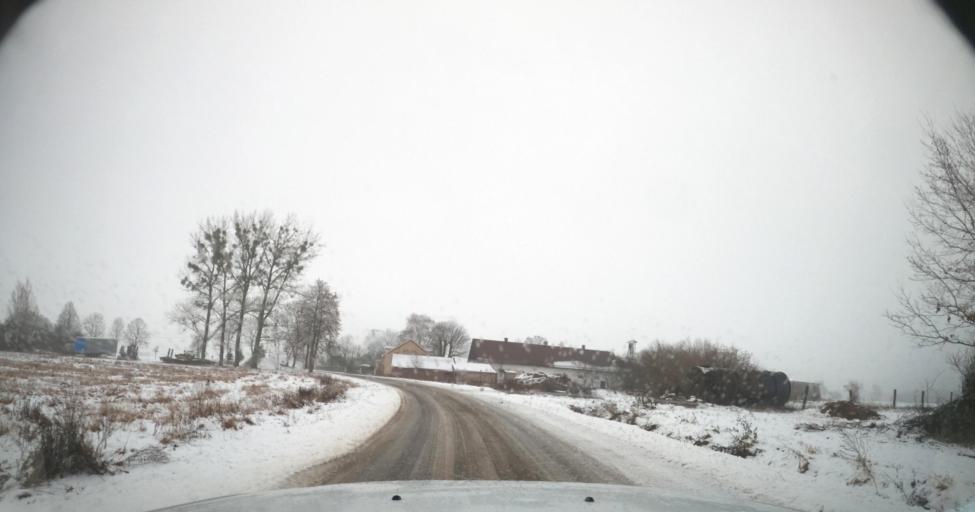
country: PL
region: West Pomeranian Voivodeship
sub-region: Powiat kamienski
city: Golczewo
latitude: 53.7939
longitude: 14.9670
